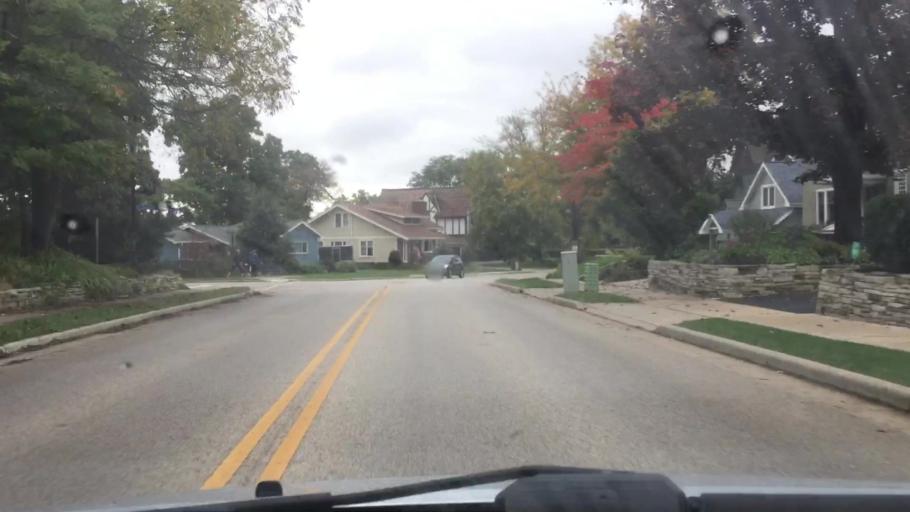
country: US
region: Wisconsin
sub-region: Waukesha County
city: Oconomowoc
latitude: 43.1190
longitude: -88.4995
